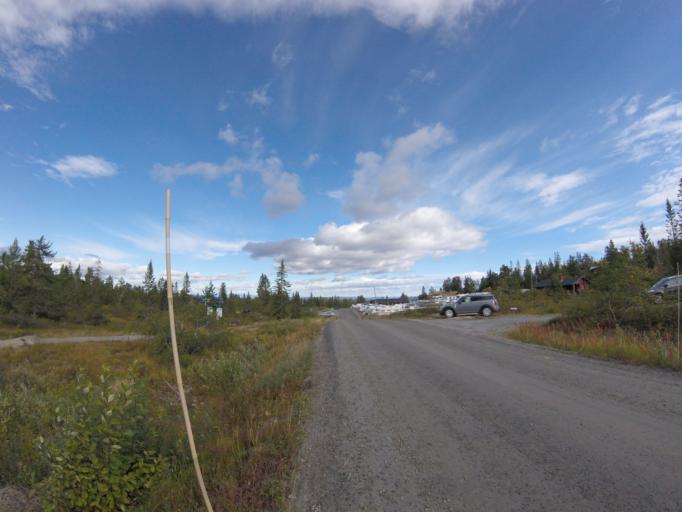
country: NO
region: Buskerud
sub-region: Flesberg
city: Lampeland
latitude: 59.7667
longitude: 9.4430
